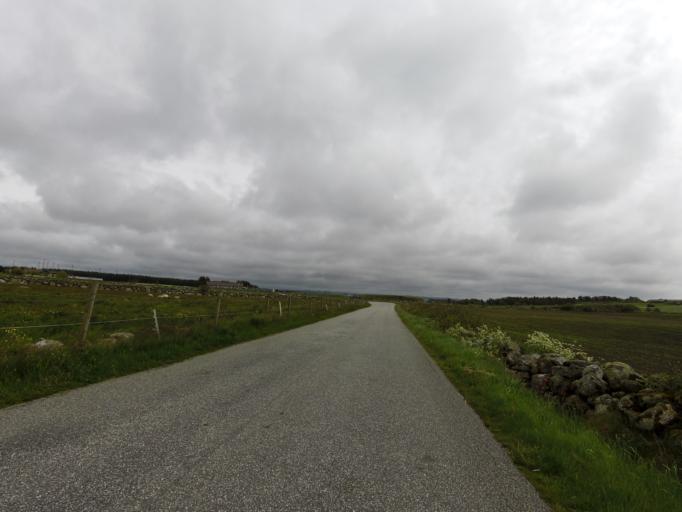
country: NO
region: Rogaland
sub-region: Ha
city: Naerbo
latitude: 58.6532
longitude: 5.5834
